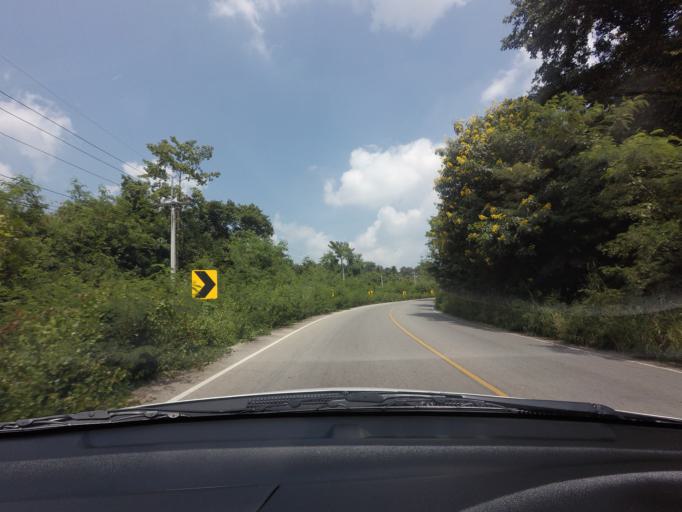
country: TH
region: Nakhon Ratchasima
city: Pak Chong
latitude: 14.6007
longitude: 101.5710
